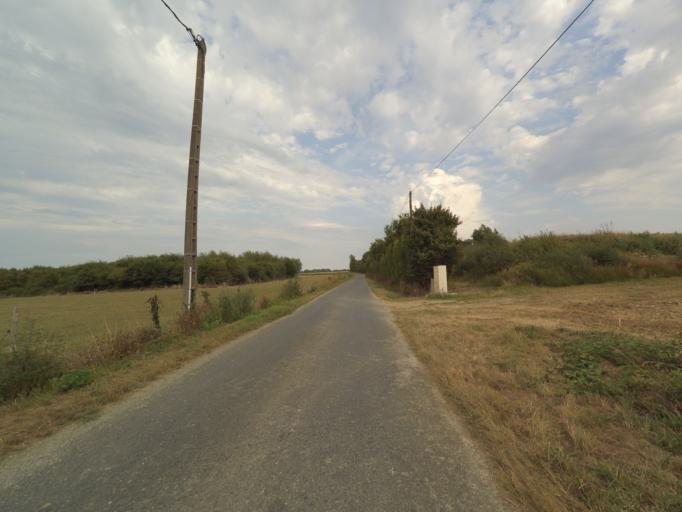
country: FR
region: Pays de la Loire
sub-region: Departement de la Vendee
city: Bouffere
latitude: 46.9816
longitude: -1.3729
